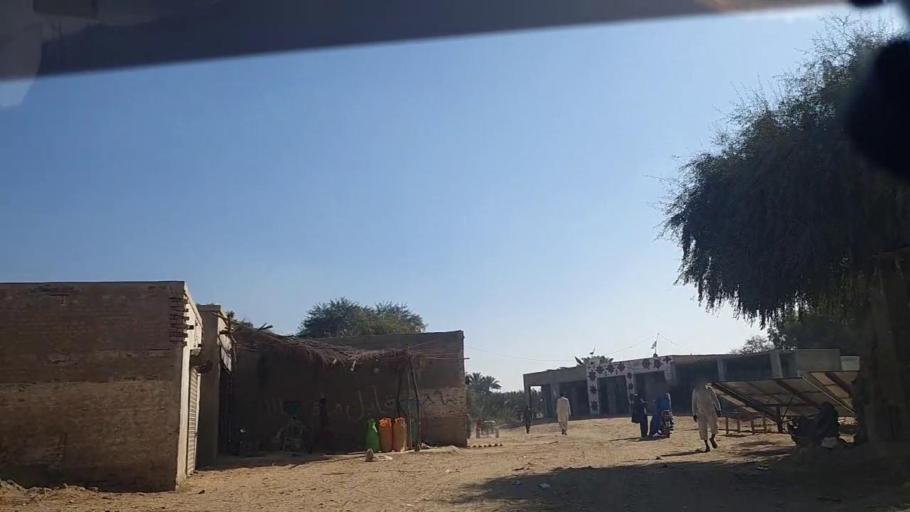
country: PK
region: Sindh
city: Khanpur
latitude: 27.6607
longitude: 69.2770
